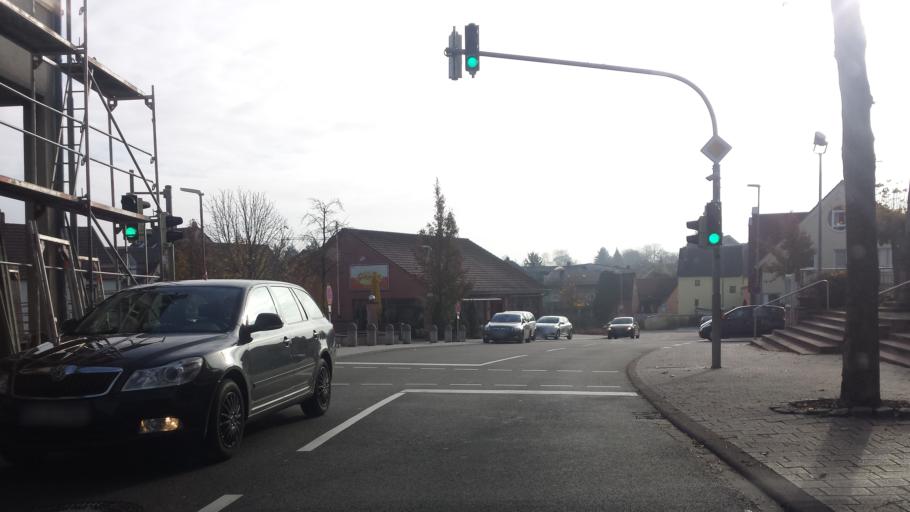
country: DE
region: Baden-Wuerttemberg
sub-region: Karlsruhe Region
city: Ubstadt-Weiher
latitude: 49.1435
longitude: 8.6678
